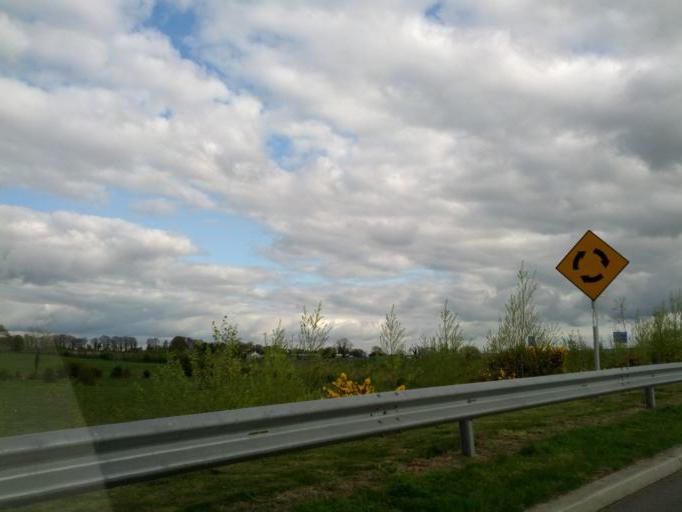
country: IE
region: Connaught
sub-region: County Galway
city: Ballinasloe
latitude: 53.3151
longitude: -8.1789
